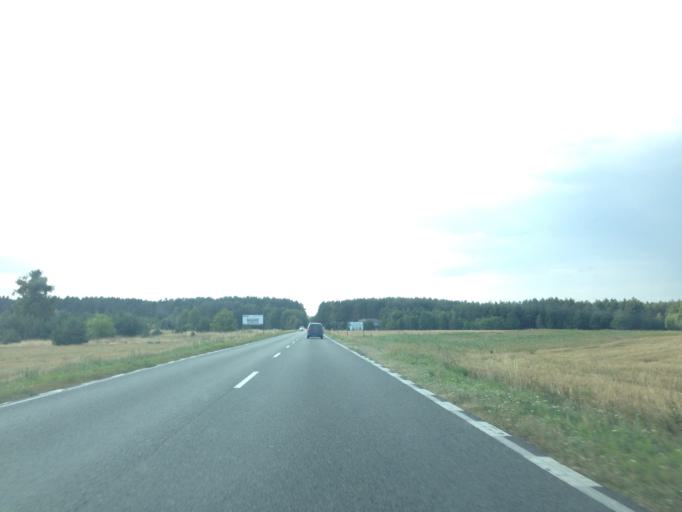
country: PL
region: Kujawsko-Pomorskie
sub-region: Powiat swiecki
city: Swiekatowo
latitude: 53.4796
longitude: 18.1409
